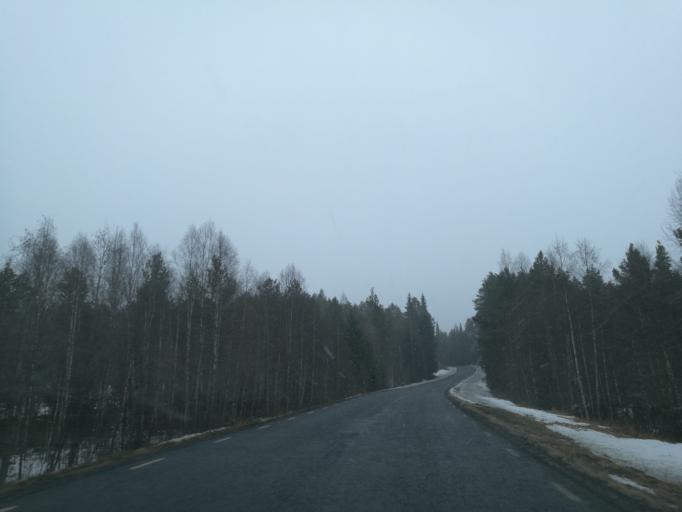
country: NO
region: Hedmark
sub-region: Grue
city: Kirkenaer
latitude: 60.6898
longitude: 12.6303
